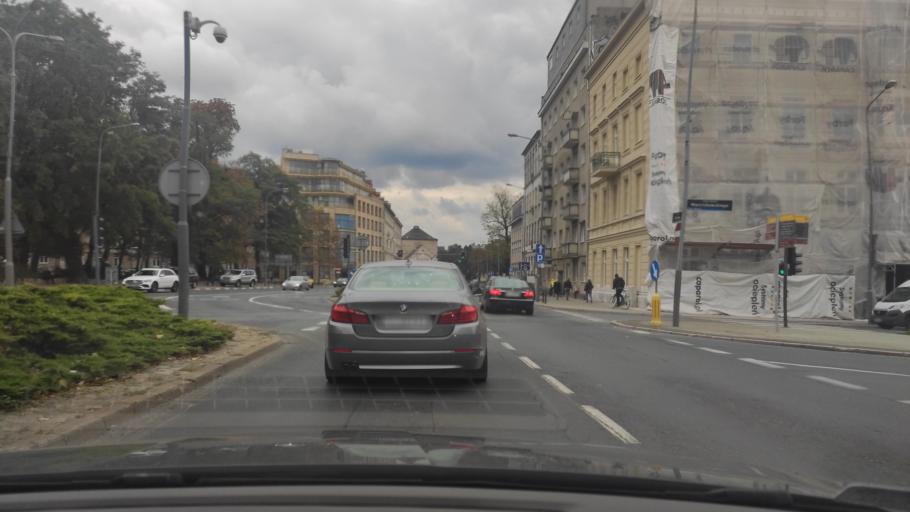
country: PL
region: Greater Poland Voivodeship
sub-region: Poznan
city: Poznan
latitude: 52.4117
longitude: 16.9295
